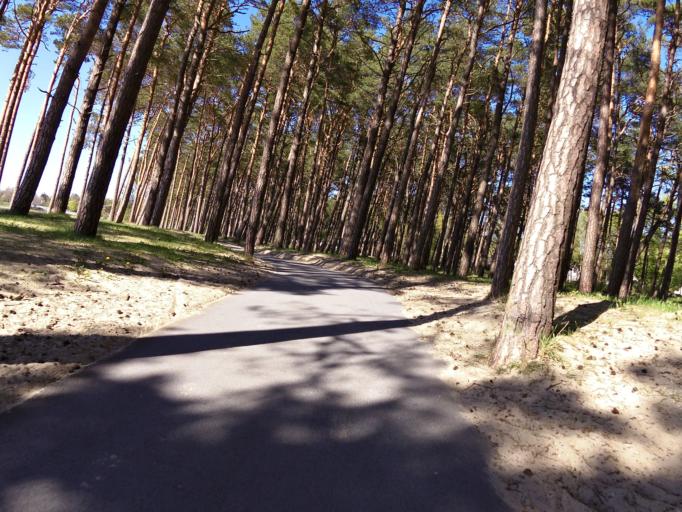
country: EE
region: Harju
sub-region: Viimsi vald
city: Viimsi
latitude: 59.4837
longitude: 24.8383
